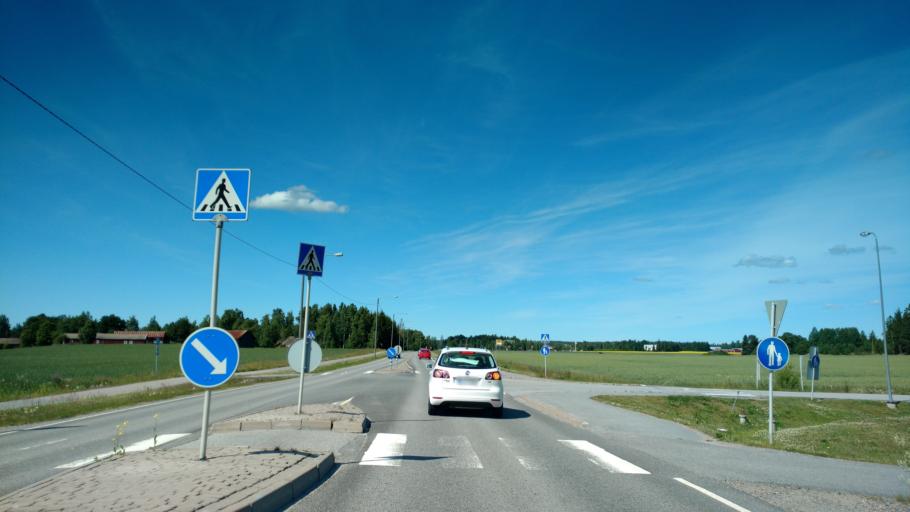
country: FI
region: Varsinais-Suomi
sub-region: Turku
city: Rusko
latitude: 60.5269
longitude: 22.2207
